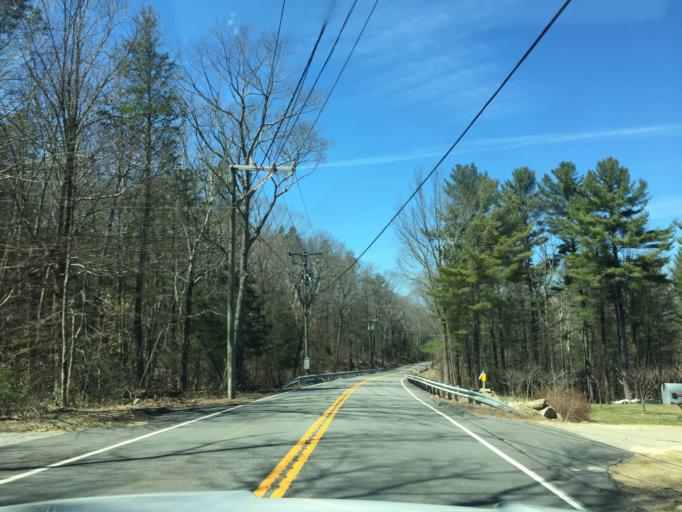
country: US
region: Massachusetts
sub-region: Hampden County
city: Holland
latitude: 41.9868
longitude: -72.1211
